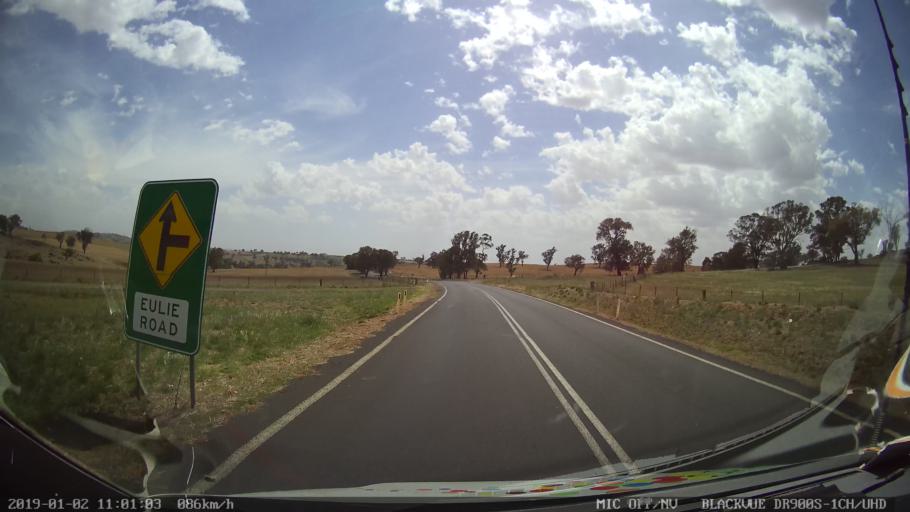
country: AU
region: New South Wales
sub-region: Young
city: Young
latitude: -34.6018
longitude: 148.3163
